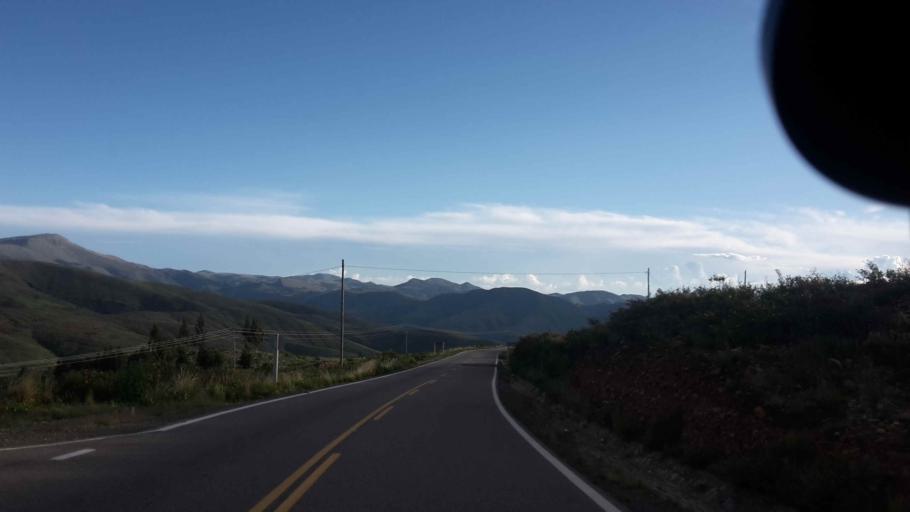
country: BO
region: Cochabamba
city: Arani
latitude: -17.5646
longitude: -65.7202
